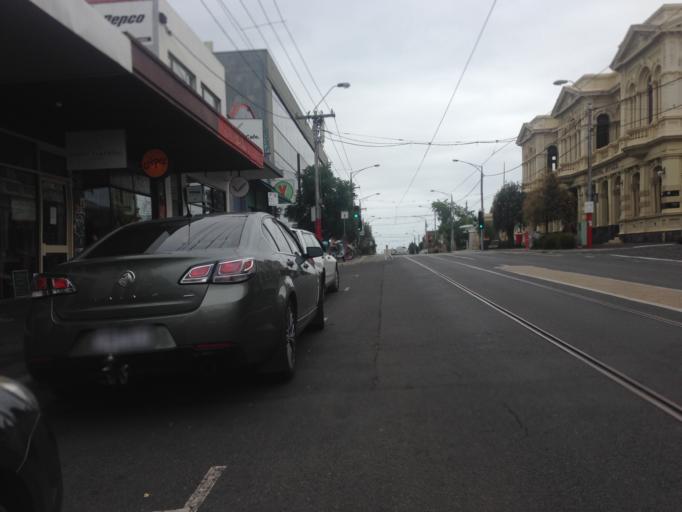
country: AU
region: Victoria
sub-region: Darebin
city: Northcote
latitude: -37.7741
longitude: 144.9981
